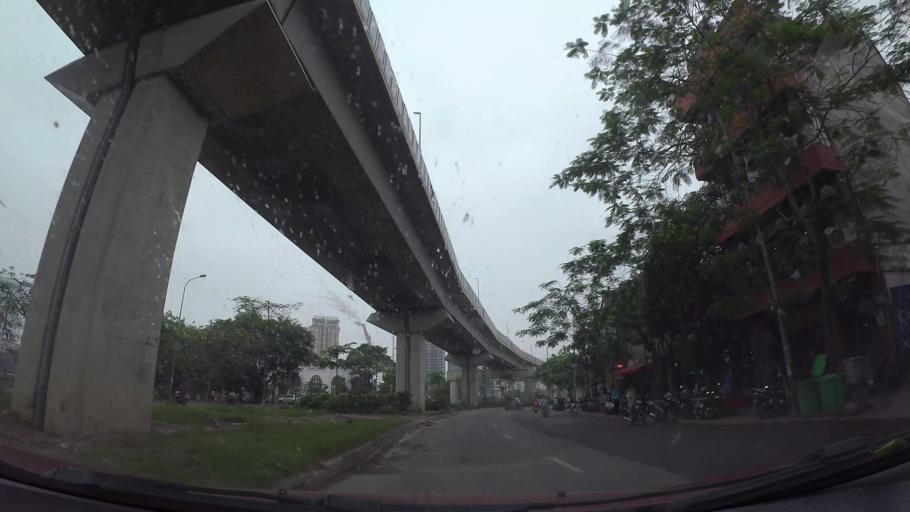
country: VN
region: Ha Noi
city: Dong Da
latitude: 21.0160
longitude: 105.8209
